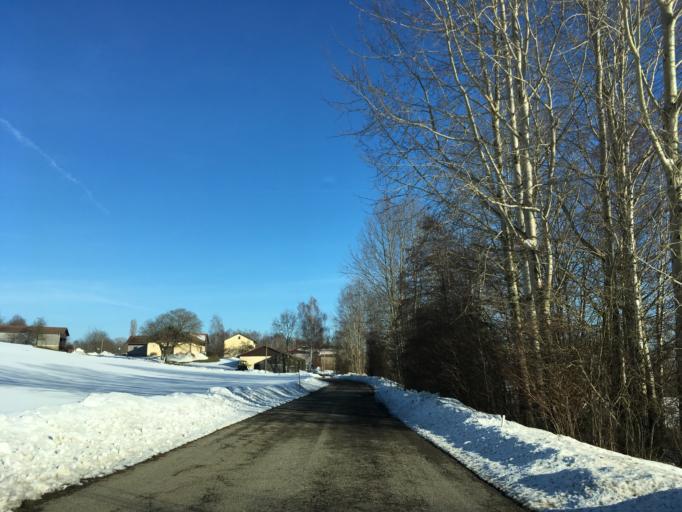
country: DE
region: Bavaria
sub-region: Upper Bavaria
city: Steinhoring
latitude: 48.1127
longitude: 12.0140
